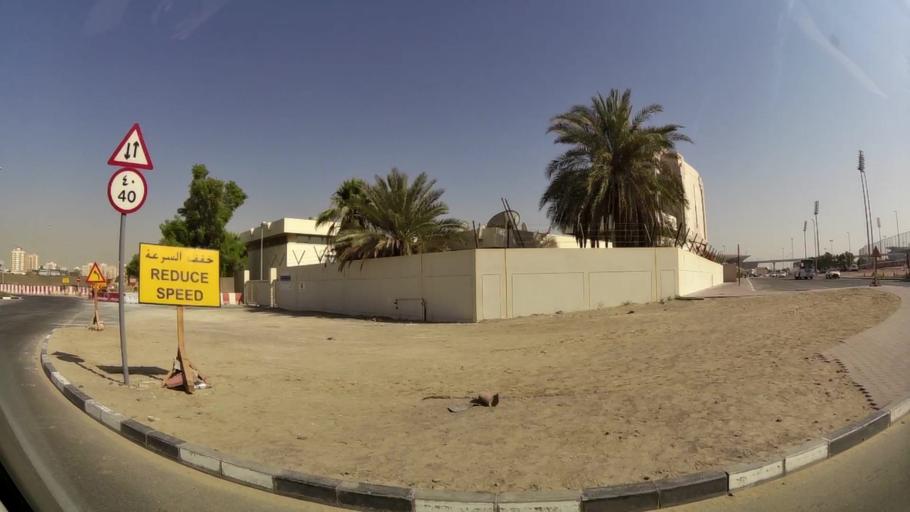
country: AE
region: Ash Shariqah
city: Sharjah
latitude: 25.2829
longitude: 55.3636
